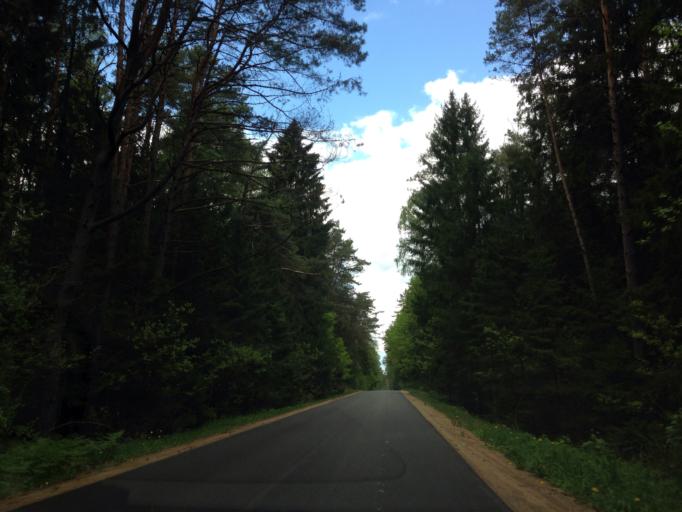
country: PL
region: Podlasie
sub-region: Powiat grajewski
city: Radzilow
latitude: 53.3412
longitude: 22.5981
